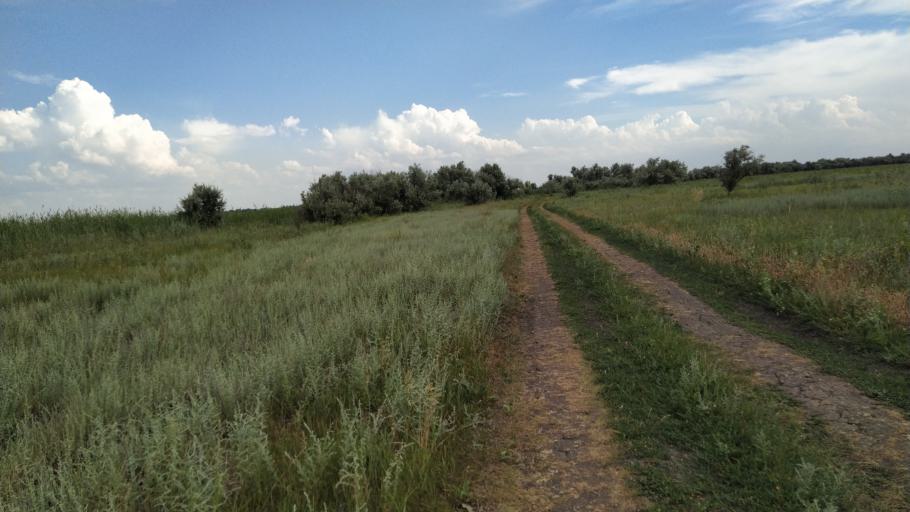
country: RU
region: Rostov
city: Kuleshovka
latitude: 47.1286
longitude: 39.6295
